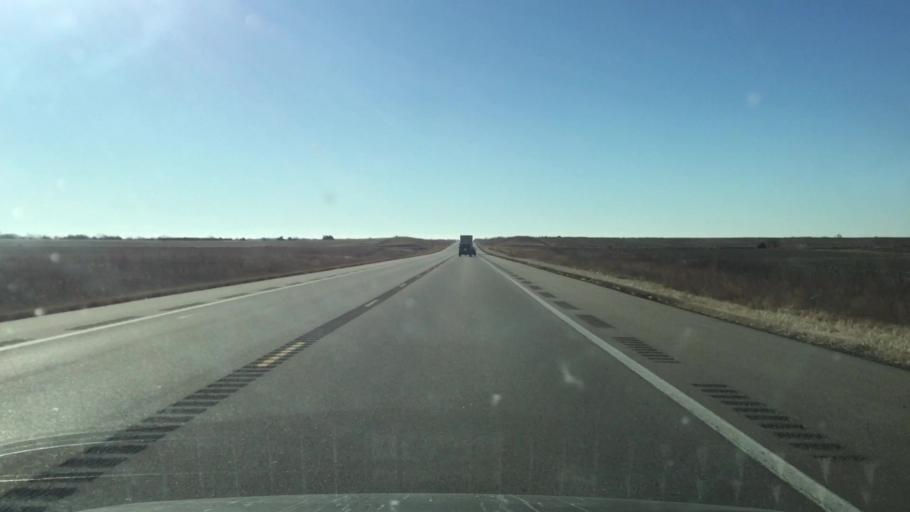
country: US
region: Kansas
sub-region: Allen County
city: Iola
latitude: 38.0570
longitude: -95.3802
